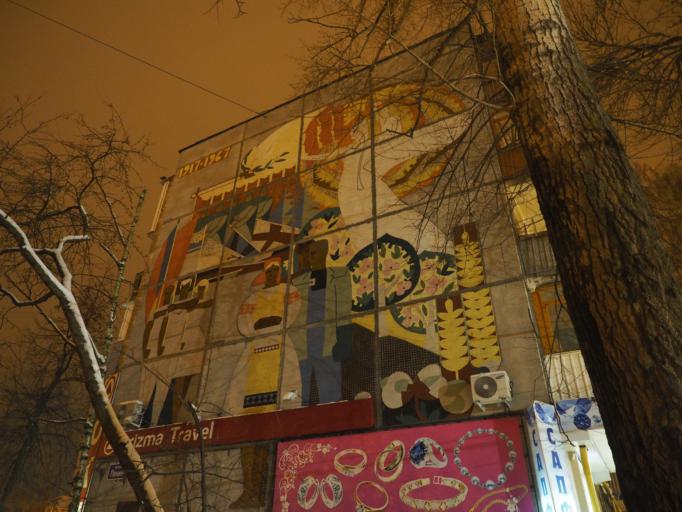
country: RU
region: Nizjnij Novgorod
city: Nizhniy Novgorod
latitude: 56.2841
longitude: 43.9254
